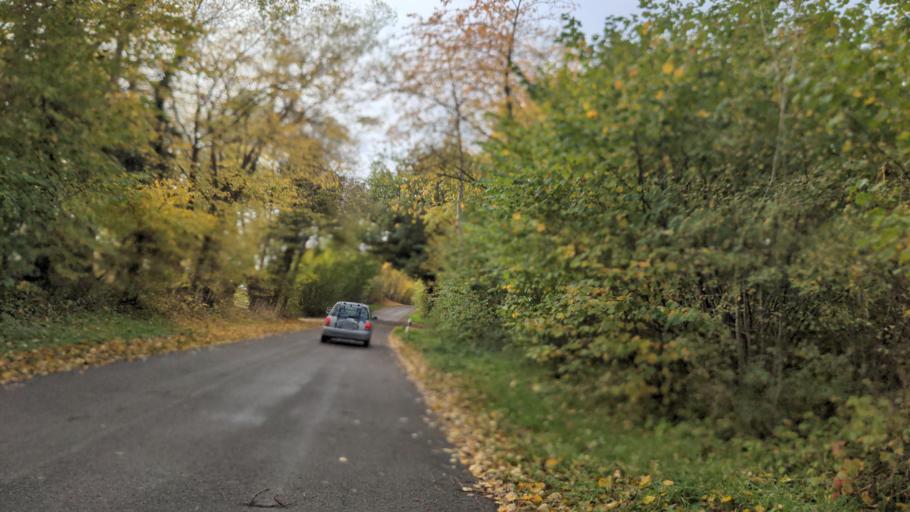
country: DE
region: Mecklenburg-Vorpommern
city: Selmsdorf
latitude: 53.9165
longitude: 10.8423
